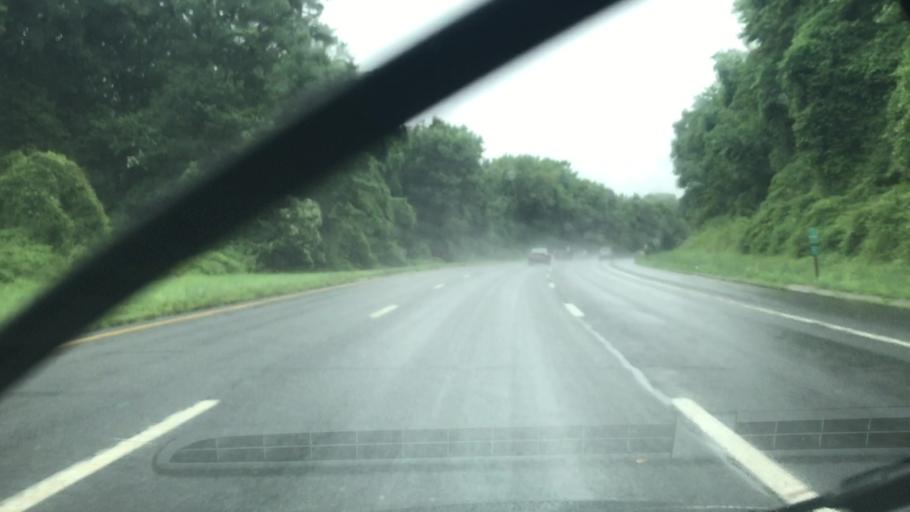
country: US
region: New York
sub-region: Westchester County
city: Yorktown Heights
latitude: 41.2440
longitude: -73.8141
